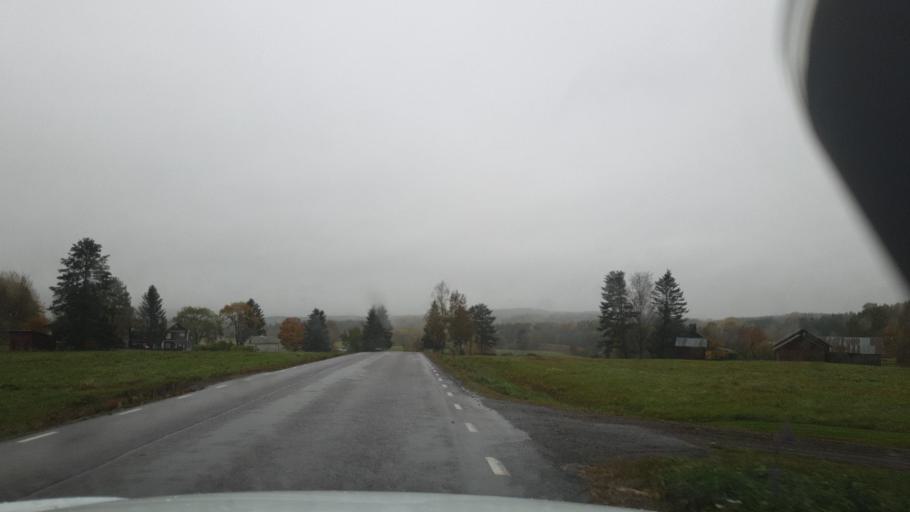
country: SE
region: Vaermland
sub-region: Eda Kommun
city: Charlottenberg
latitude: 59.7864
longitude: 12.1583
